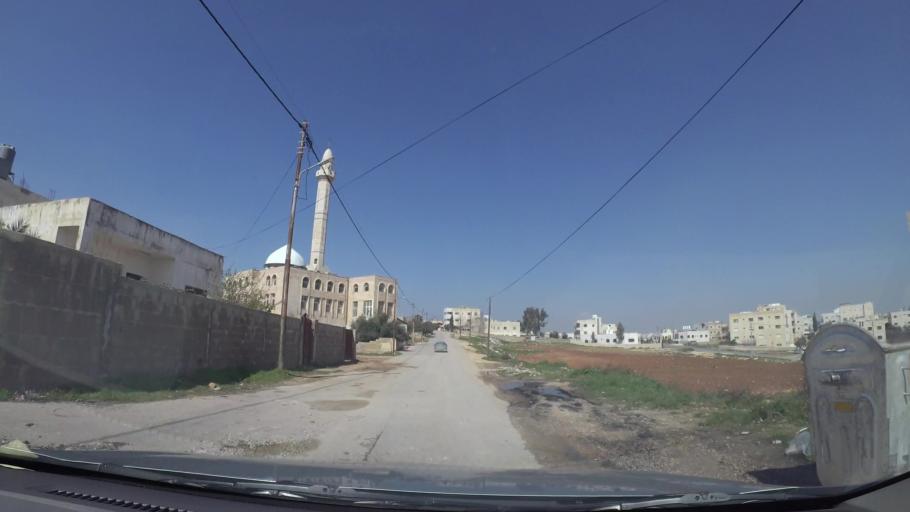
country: JO
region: Amman
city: Al Bunayyat ash Shamaliyah
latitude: 31.8935
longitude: 35.8956
